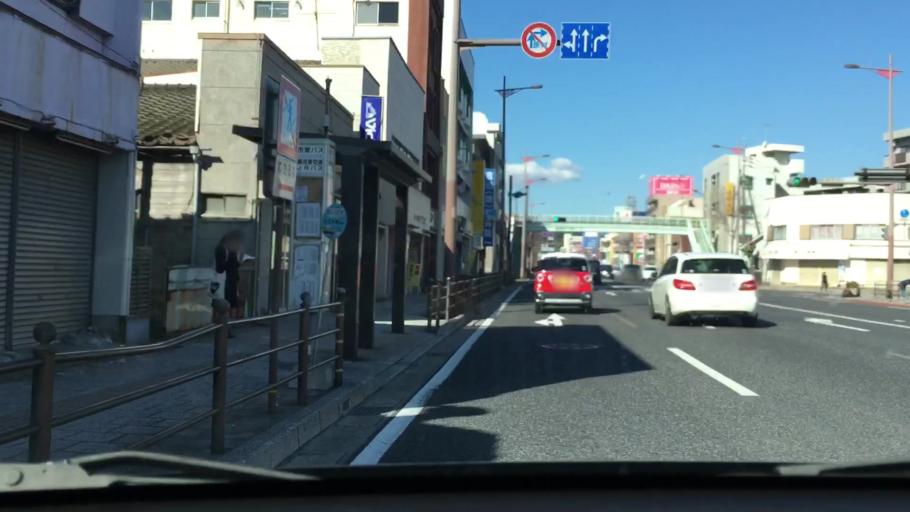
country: JP
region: Kagoshima
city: Kagoshima-shi
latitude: 31.6104
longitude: 130.5337
